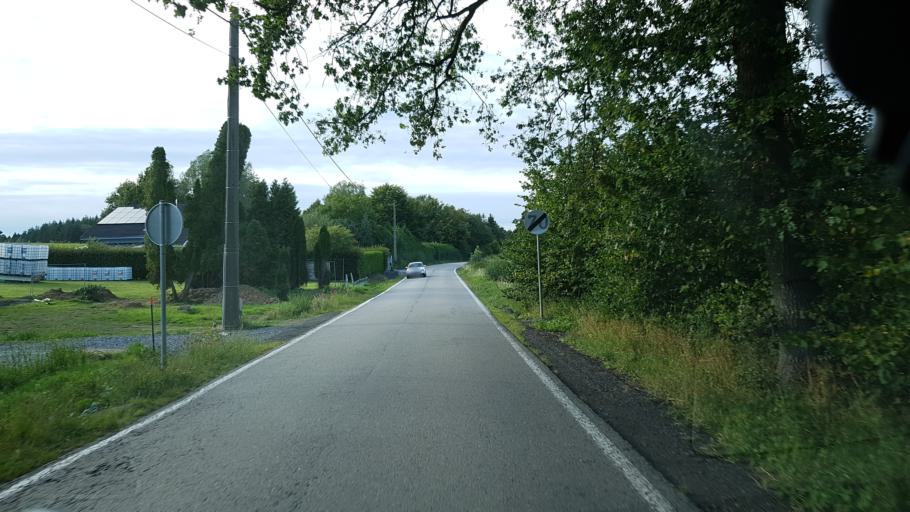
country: BE
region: Wallonia
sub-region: Province de Liege
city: Theux
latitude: 50.4995
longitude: 5.7681
